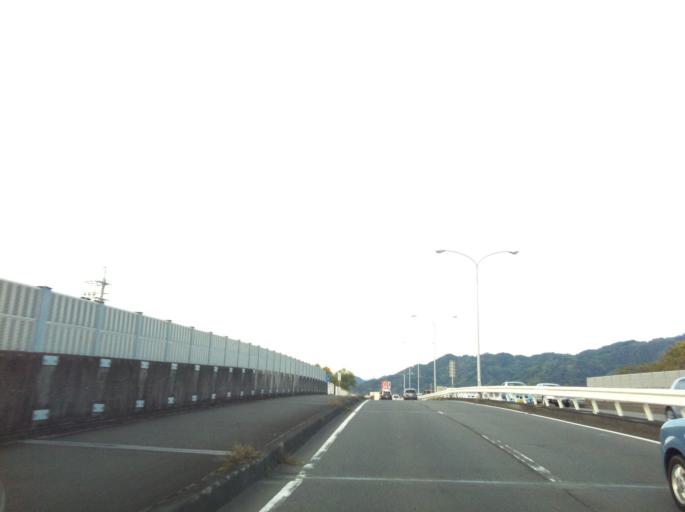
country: JP
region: Shizuoka
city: Yaizu
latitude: 34.8707
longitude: 138.2994
